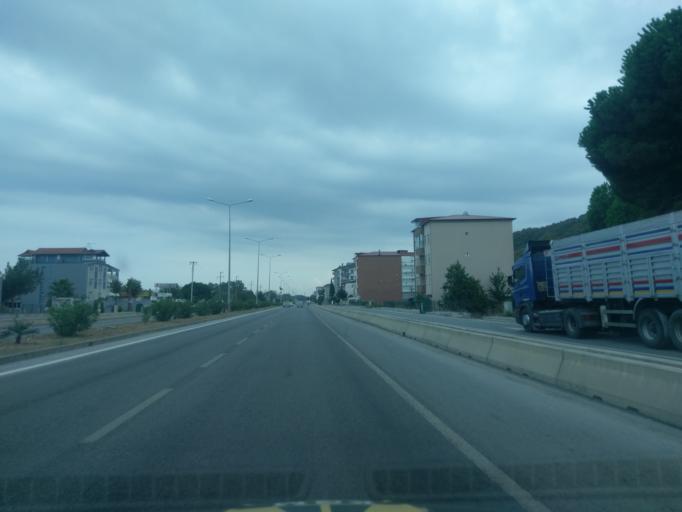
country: TR
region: Samsun
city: Taflan
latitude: 41.3860
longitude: 36.2079
